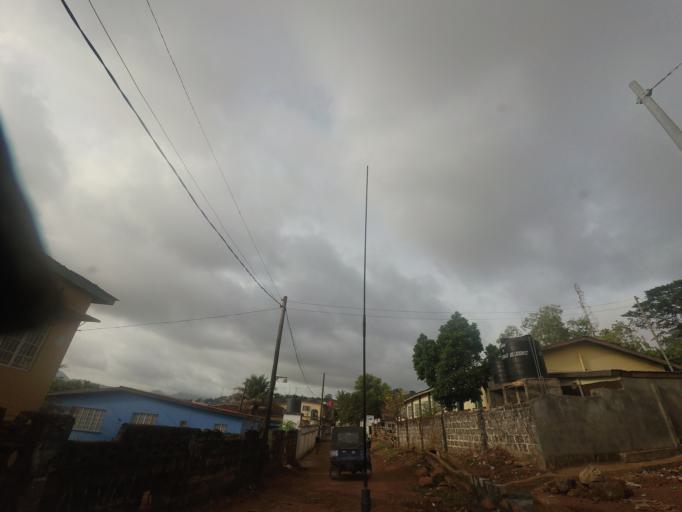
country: SL
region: Western Area
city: Freetown
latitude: 8.4898
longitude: -13.2650
